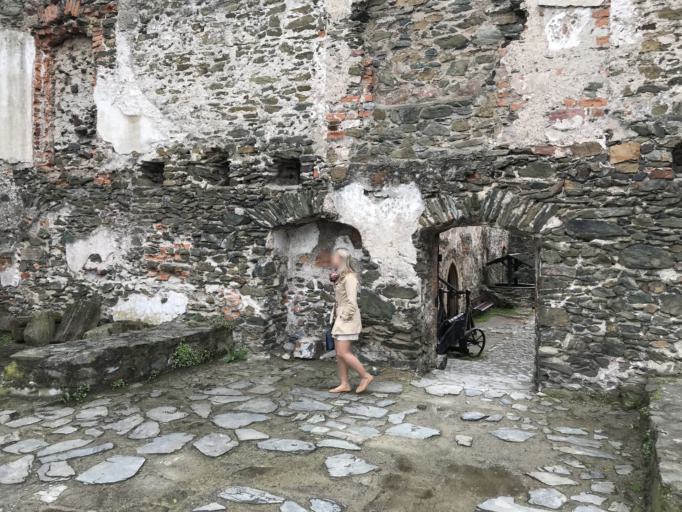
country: PL
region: Lower Silesian Voivodeship
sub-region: Powiat jaworski
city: Bolkow
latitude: 50.9222
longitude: 16.0982
